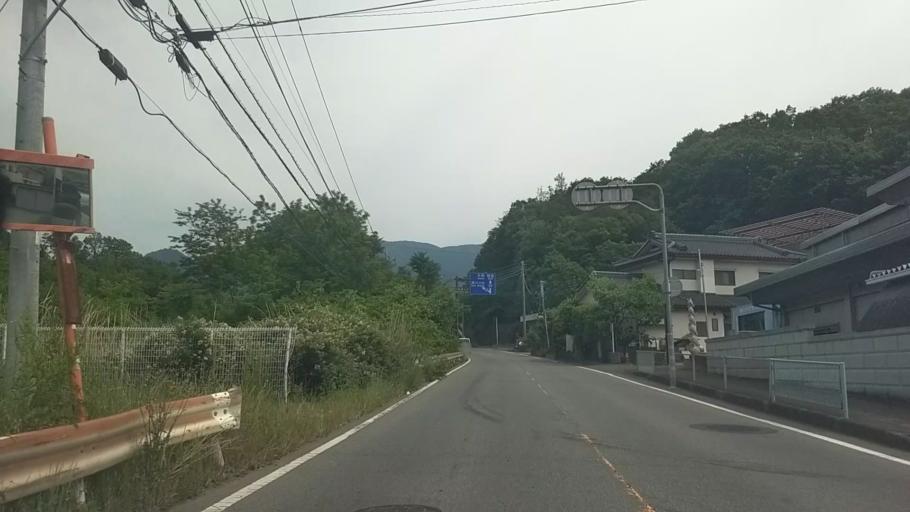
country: JP
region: Yamanashi
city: Isawa
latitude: 35.5934
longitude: 138.5886
